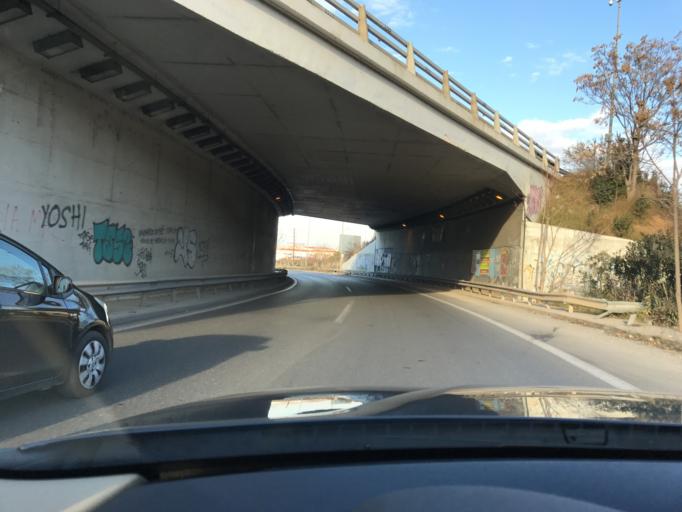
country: GR
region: Central Macedonia
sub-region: Nomos Thessalonikis
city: Efkarpia
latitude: 40.6785
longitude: 22.9589
